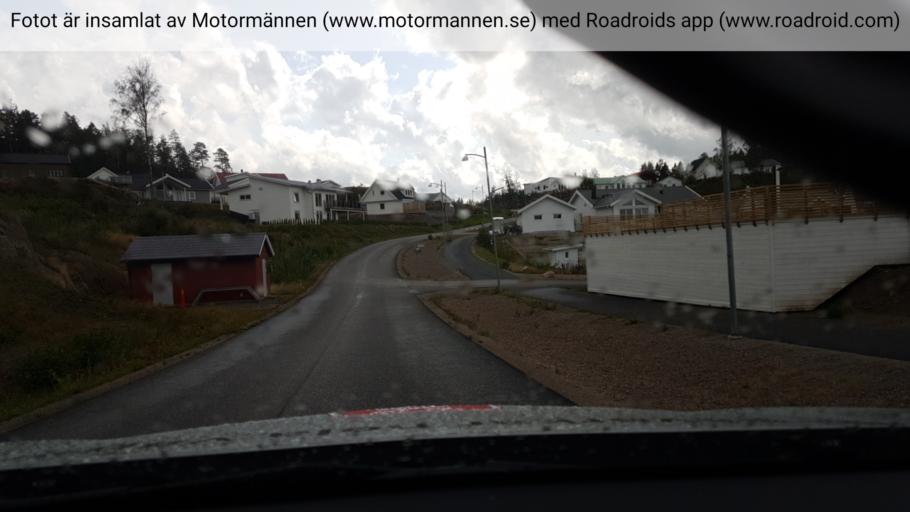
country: SE
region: Vaestra Goetaland
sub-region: Uddevalla Kommun
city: Uddevalla
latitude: 58.3212
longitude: 11.8743
